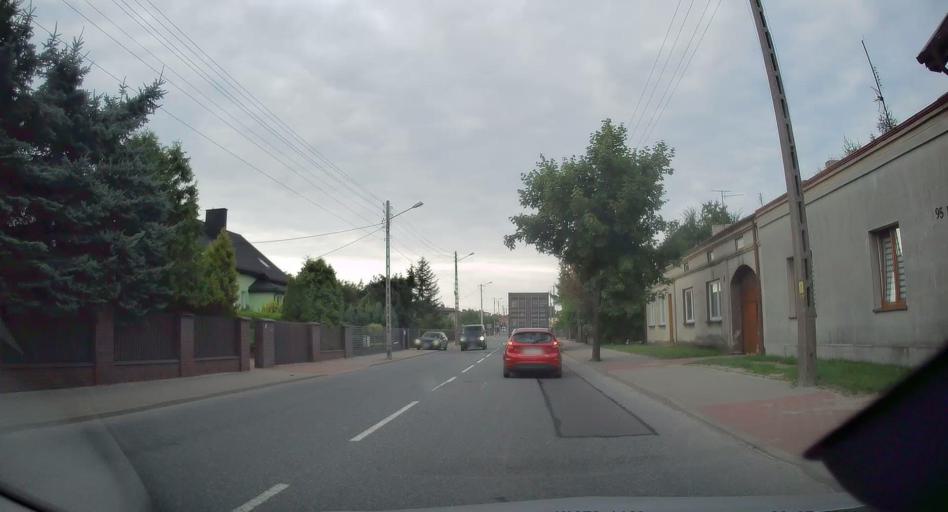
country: PL
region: Lodz Voivodeship
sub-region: Powiat radomszczanski
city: Kamiensk
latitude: 51.1977
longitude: 19.4993
